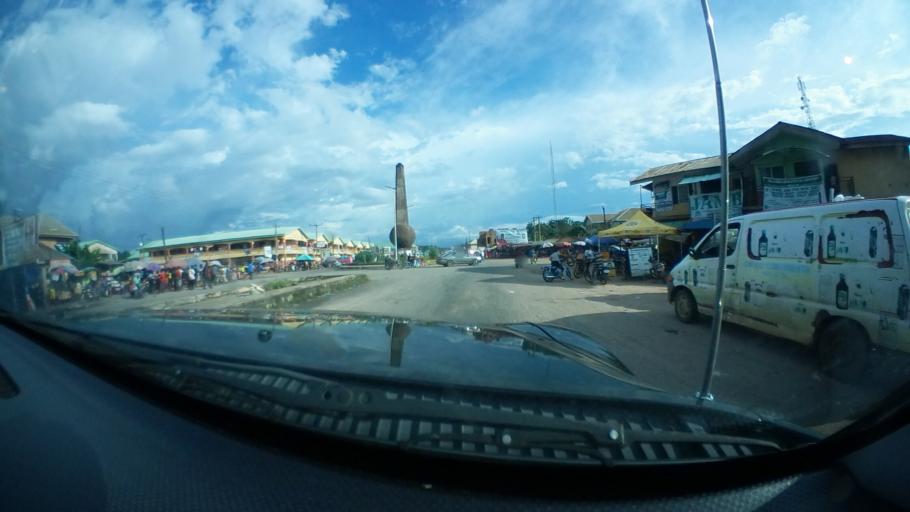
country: NG
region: Imo
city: Orodo
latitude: 5.6710
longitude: 7.0142
